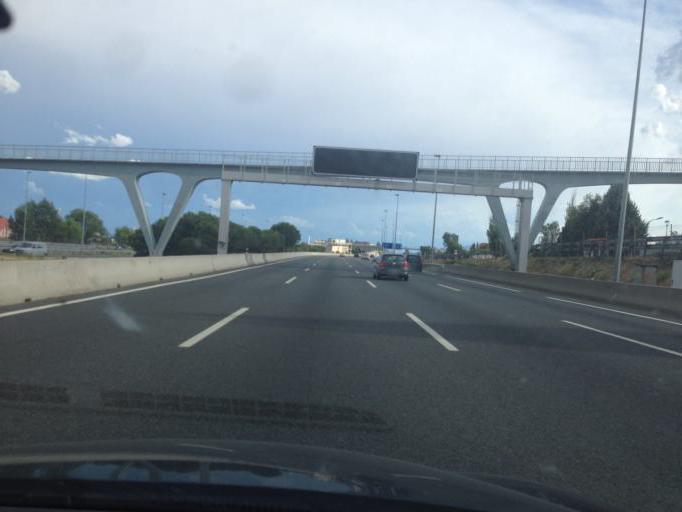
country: ES
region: Madrid
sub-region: Provincia de Madrid
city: Las Matas
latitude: 40.5317
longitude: -3.8876
